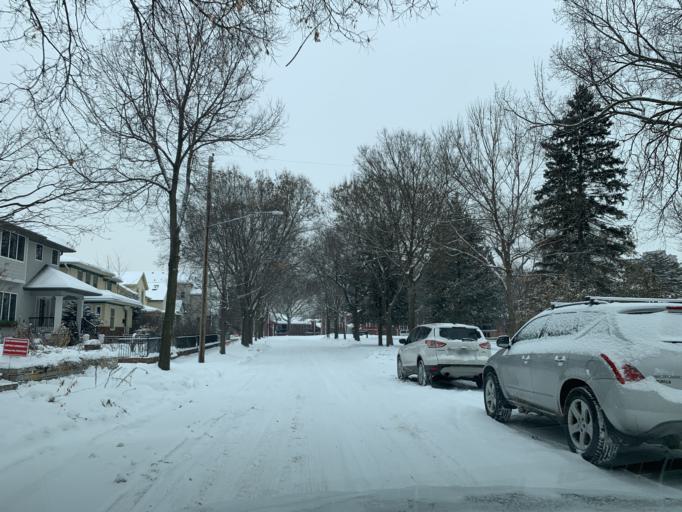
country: US
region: Minnesota
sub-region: Hennepin County
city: Saint Louis Park
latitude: 44.9501
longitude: -93.3237
